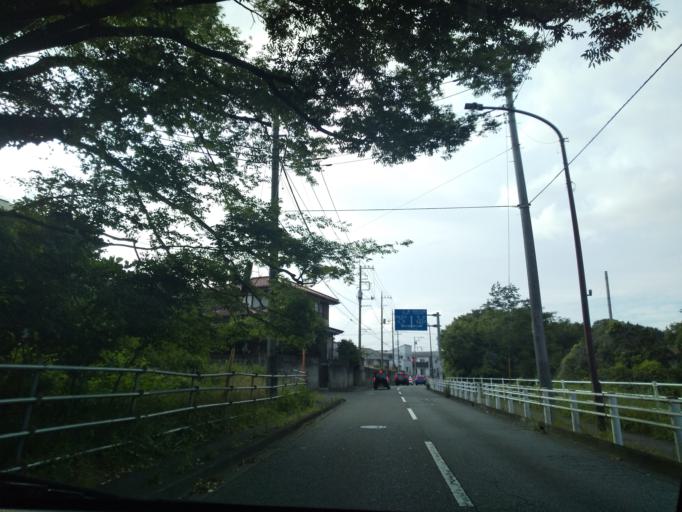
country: JP
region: Kanagawa
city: Zama
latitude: 35.5272
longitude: 139.3831
